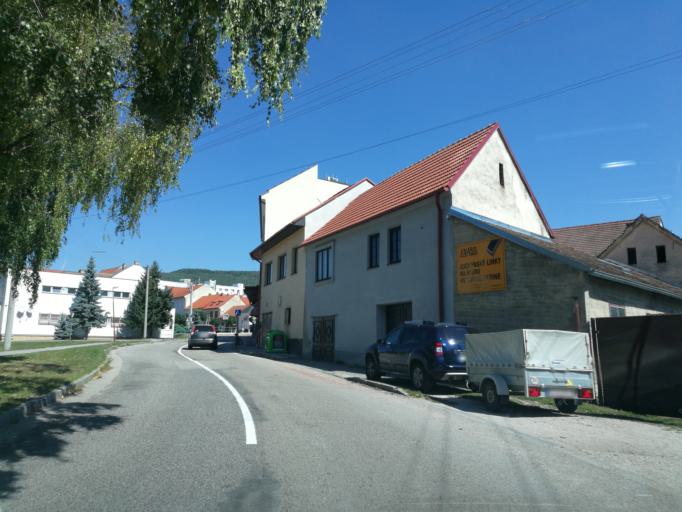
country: SK
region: Nitriansky
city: Brezova pod Bradlom
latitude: 48.6641
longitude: 17.5393
